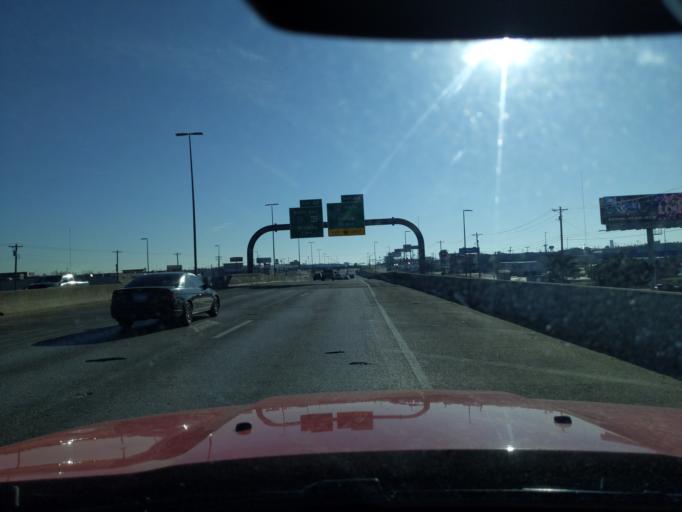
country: US
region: Oklahoma
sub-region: Cleveland County
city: Moore
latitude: 35.3919
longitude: -97.5127
